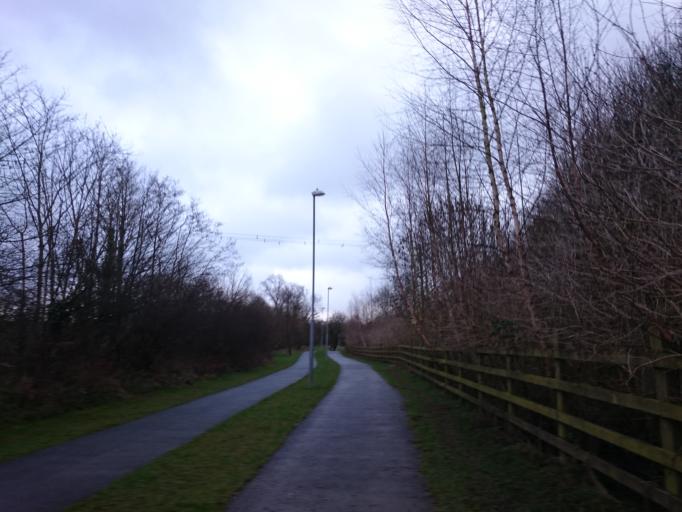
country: IE
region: Leinster
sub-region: Kilkenny
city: Kilkenny
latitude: 52.6678
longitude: -7.2605
